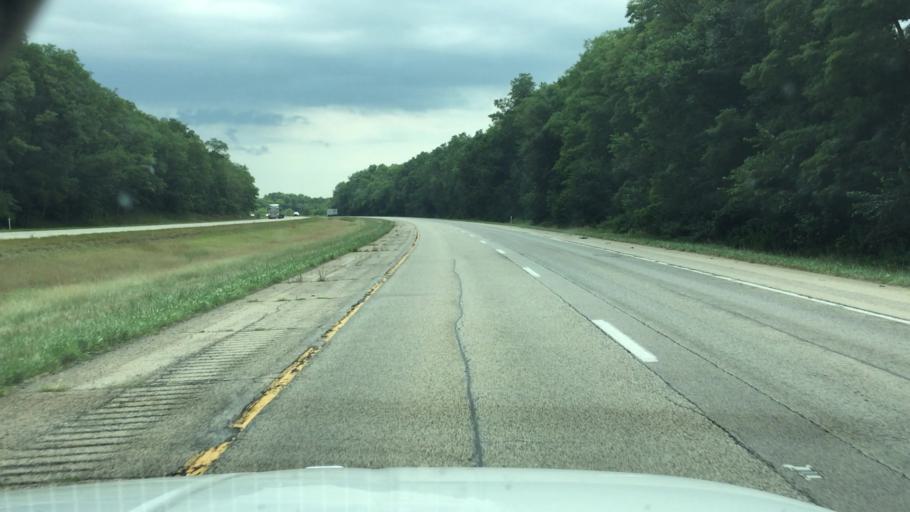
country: US
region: Illinois
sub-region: Peoria County
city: Hanna City
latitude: 40.8051
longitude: -89.8276
